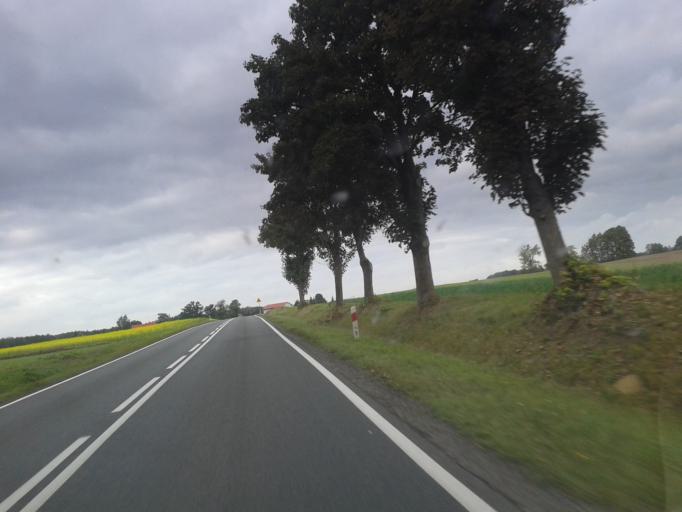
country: PL
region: Kujawsko-Pomorskie
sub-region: Powiat sepolenski
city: Sepolno Krajenskie
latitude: 53.4817
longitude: 17.5208
